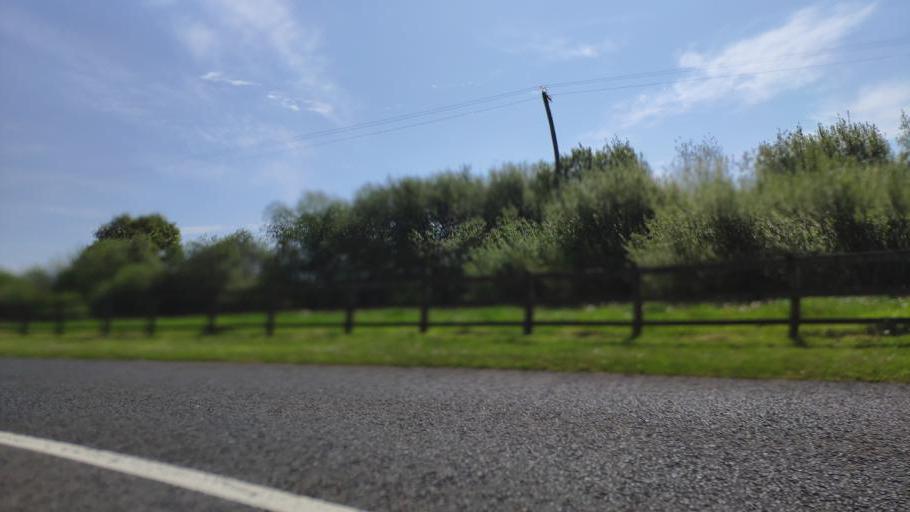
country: IE
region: Munster
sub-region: County Cork
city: Blarney
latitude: 51.9296
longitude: -8.5543
